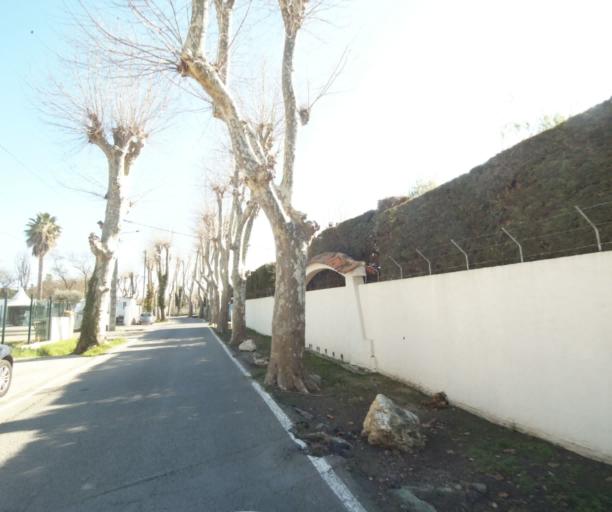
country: FR
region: Provence-Alpes-Cote d'Azur
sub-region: Departement des Alpes-Maritimes
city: Biot
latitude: 43.6133
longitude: 7.1180
